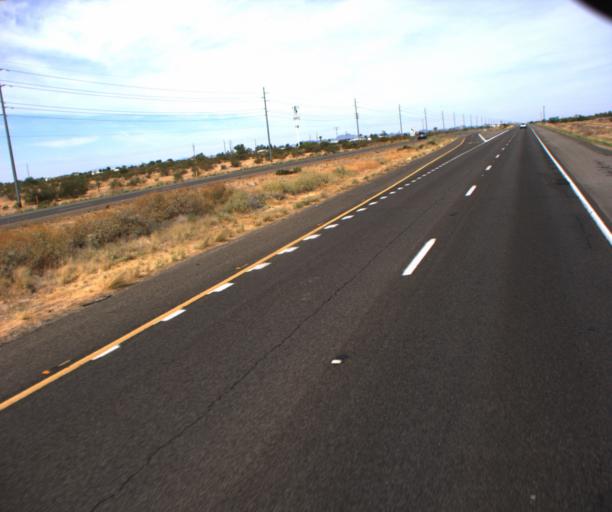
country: US
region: Arizona
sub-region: Maricopa County
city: Sun City West
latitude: 33.7518
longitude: -112.4950
